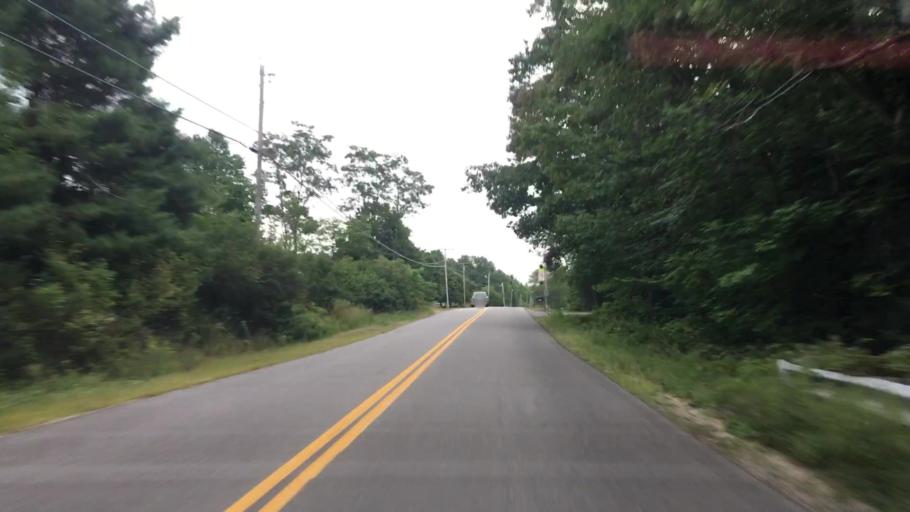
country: US
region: Maine
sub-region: Cumberland County
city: Yarmouth
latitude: 43.8981
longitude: -70.1968
